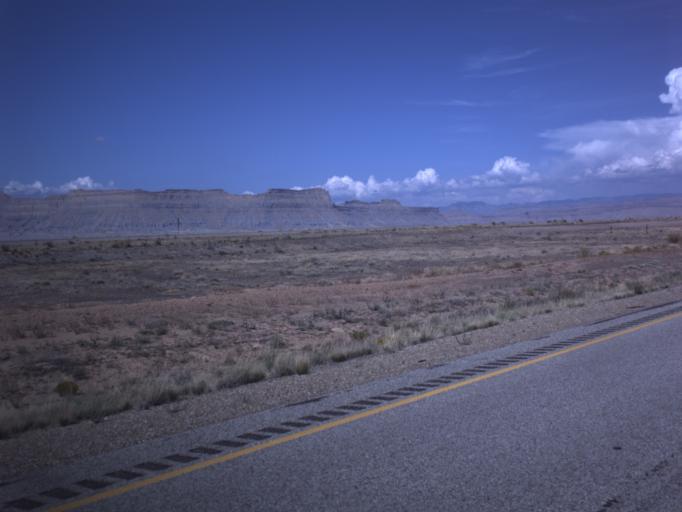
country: US
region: Utah
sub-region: Carbon County
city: East Carbon City
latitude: 38.9691
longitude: -110.2662
